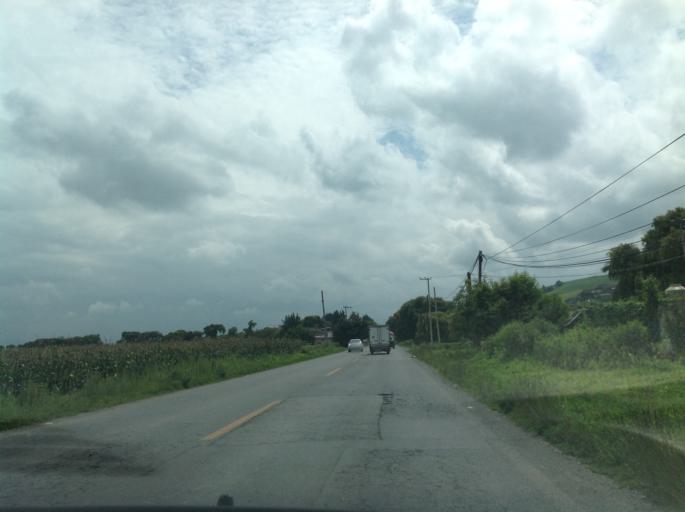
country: MX
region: Mexico
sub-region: Rayon
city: Colonia Emiliano Zapata
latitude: 19.1094
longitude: -99.5723
